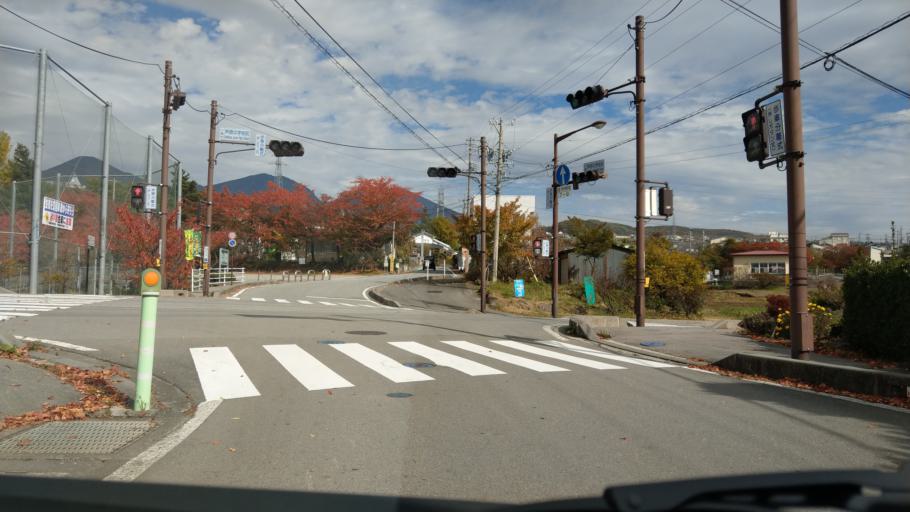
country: JP
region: Nagano
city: Komoro
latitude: 36.3328
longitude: 138.4139
